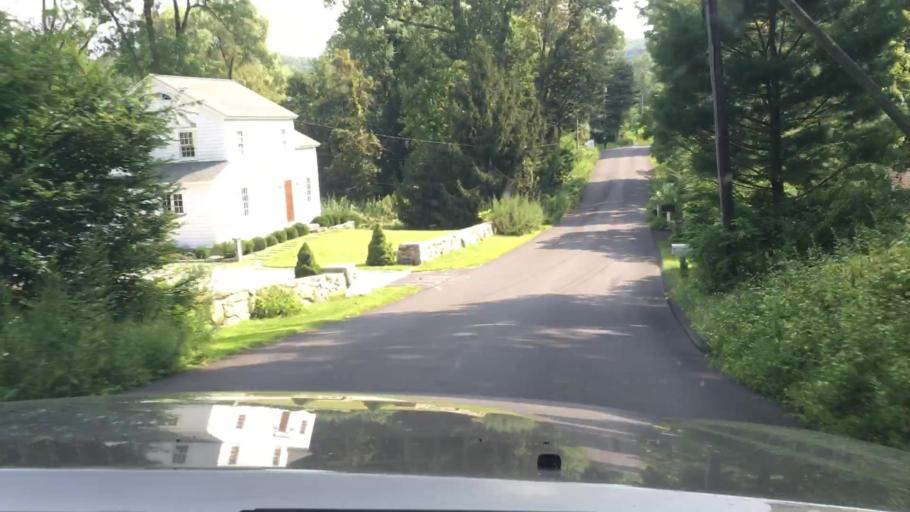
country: US
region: Connecticut
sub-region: Fairfield County
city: Georgetown
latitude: 41.2684
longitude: -73.4492
